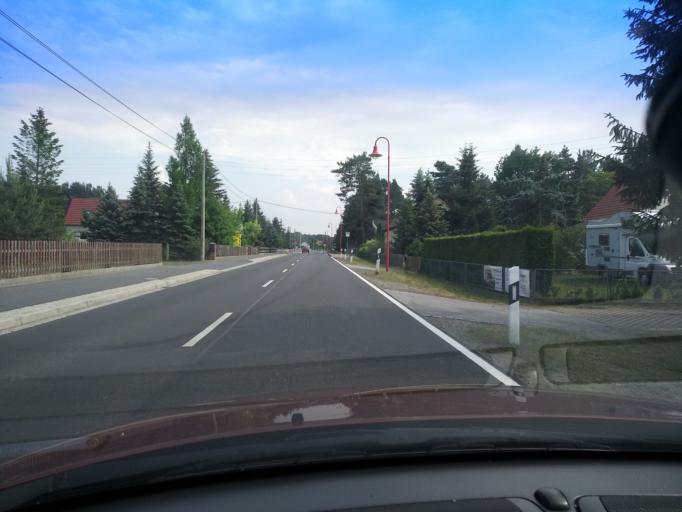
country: DE
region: Saxony
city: Mucka
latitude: 51.3355
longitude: 14.6881
